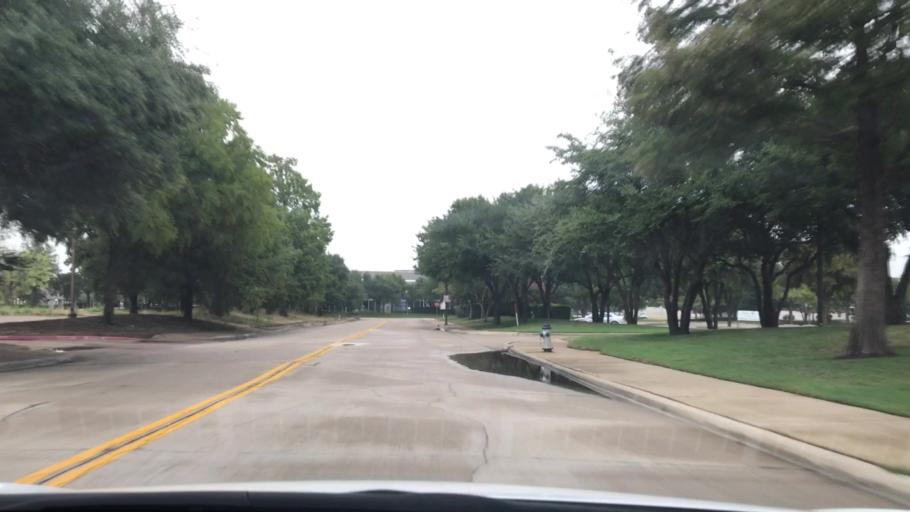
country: US
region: Texas
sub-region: Dallas County
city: Coppell
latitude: 32.9336
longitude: -97.0143
